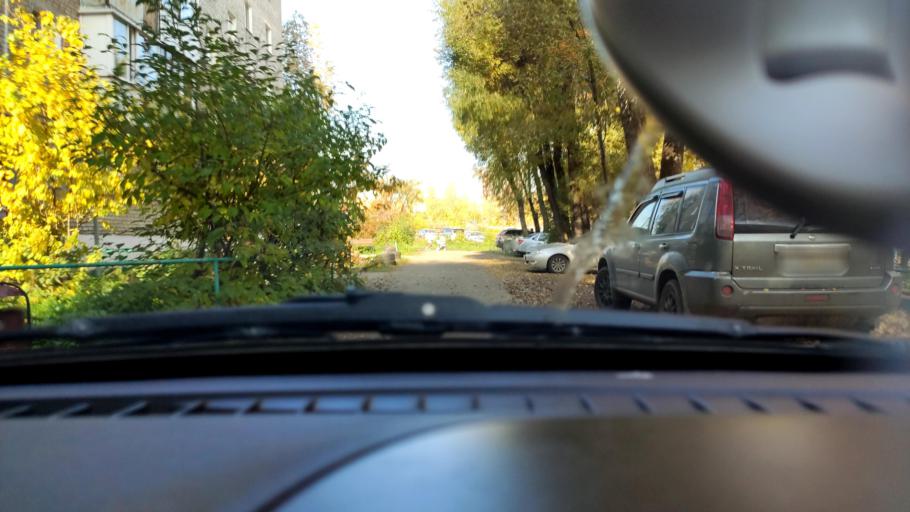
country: RU
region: Perm
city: Perm
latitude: 58.0159
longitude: 56.3010
